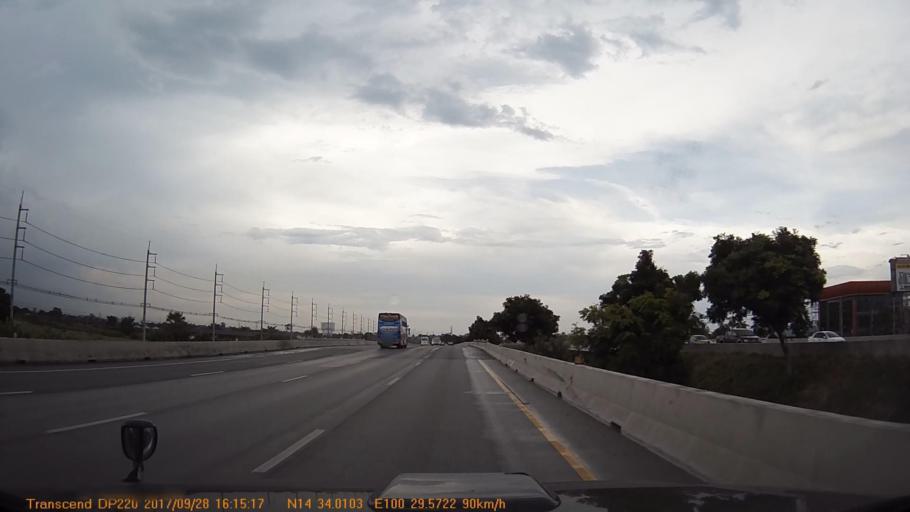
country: TH
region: Ang Thong
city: Ang Thong
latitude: 14.5674
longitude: 100.4926
